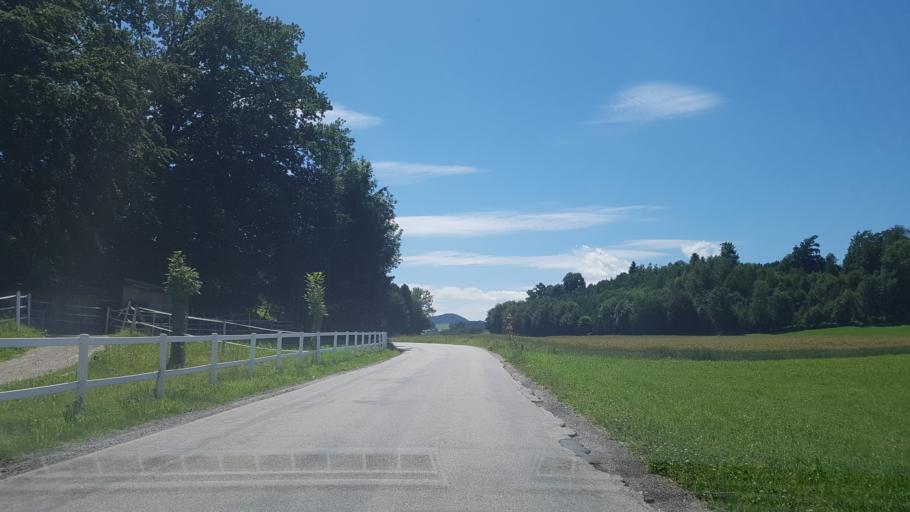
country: AT
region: Salzburg
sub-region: Politischer Bezirk Salzburg-Umgebung
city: Schleedorf
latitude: 48.0042
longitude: 13.1589
